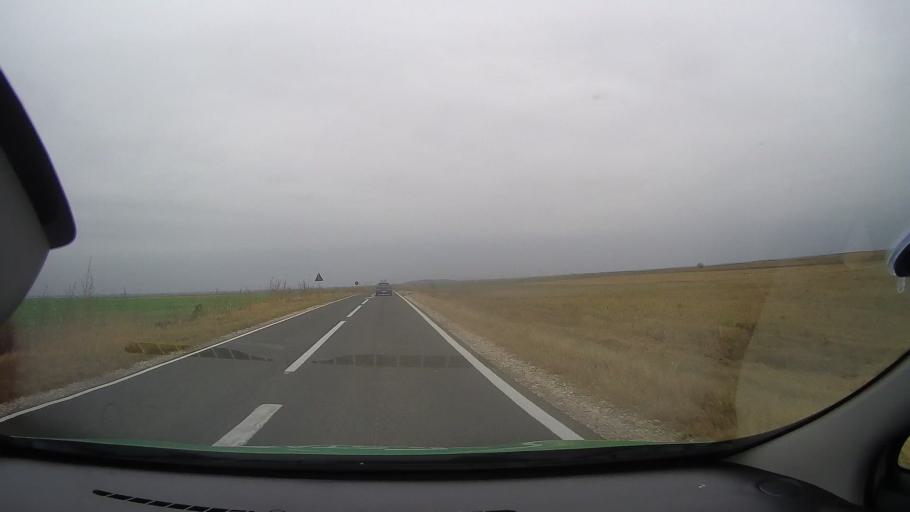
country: RO
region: Constanta
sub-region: Comuna Ciobanu
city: Ciobanu
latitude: 44.7021
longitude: 28.0205
